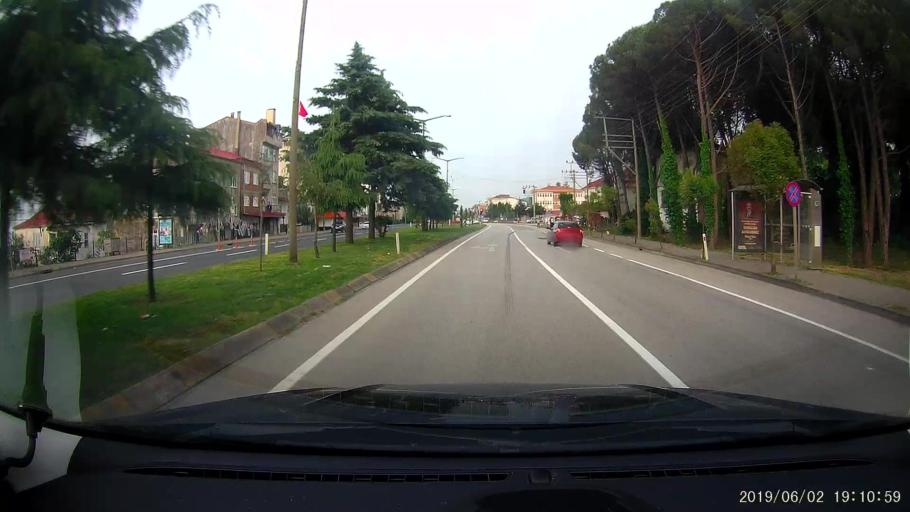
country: TR
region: Ordu
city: Gulyali
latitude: 40.9672
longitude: 38.0548
